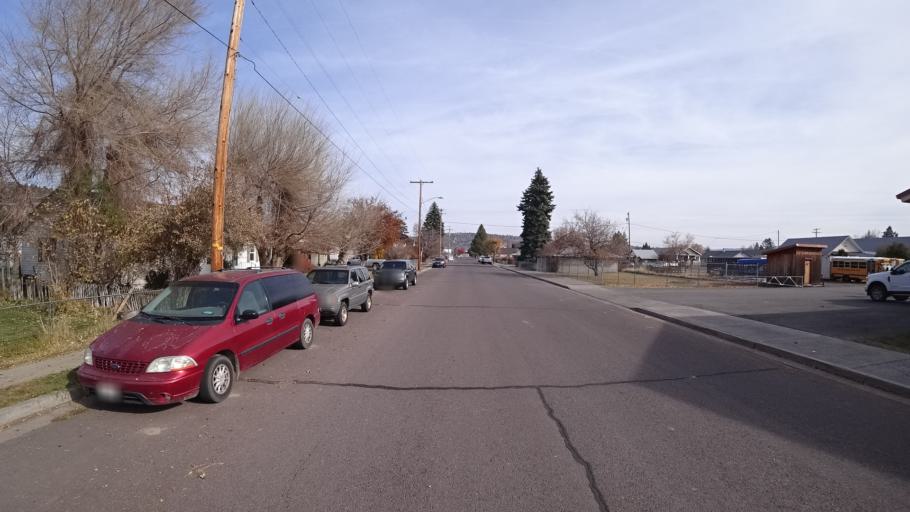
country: US
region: Oregon
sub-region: Klamath County
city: Klamath Falls
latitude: 41.9642
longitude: -121.9236
